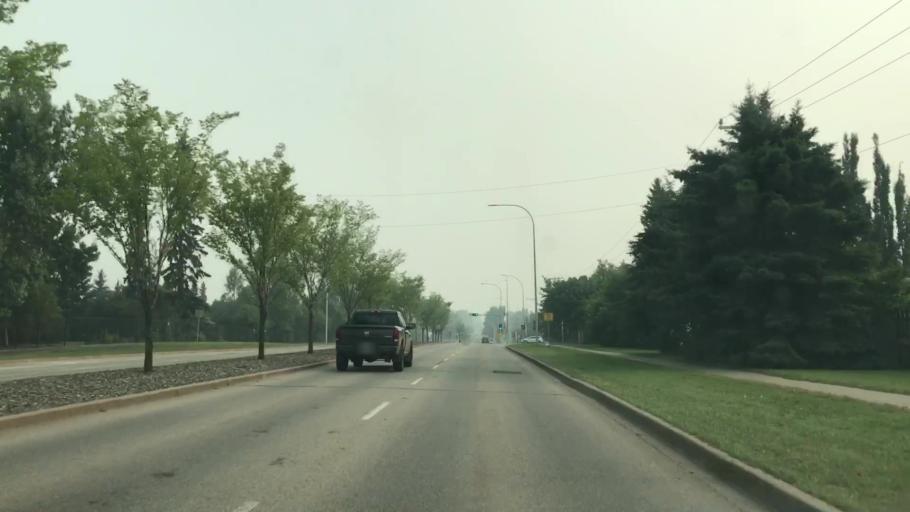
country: CA
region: Alberta
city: Sherwood Park
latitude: 53.5228
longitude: -113.3201
